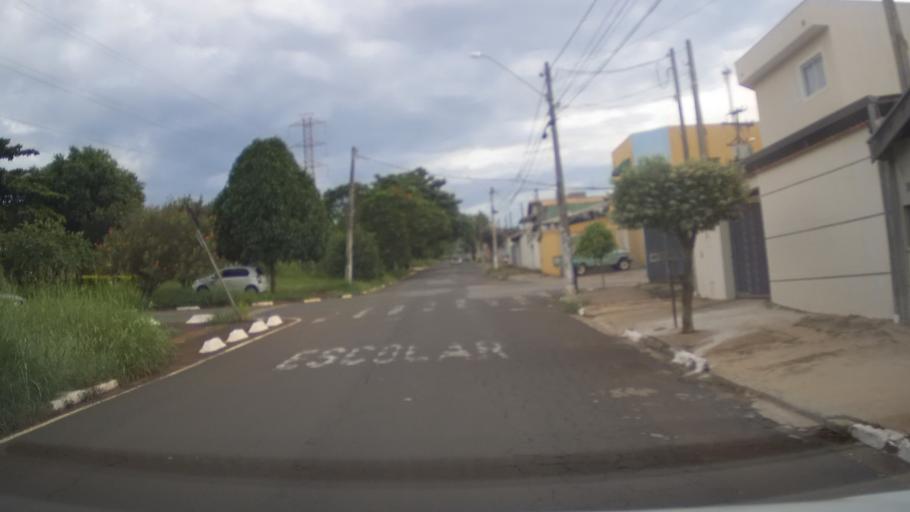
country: BR
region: Sao Paulo
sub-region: Campinas
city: Campinas
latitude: -22.8855
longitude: -47.1284
